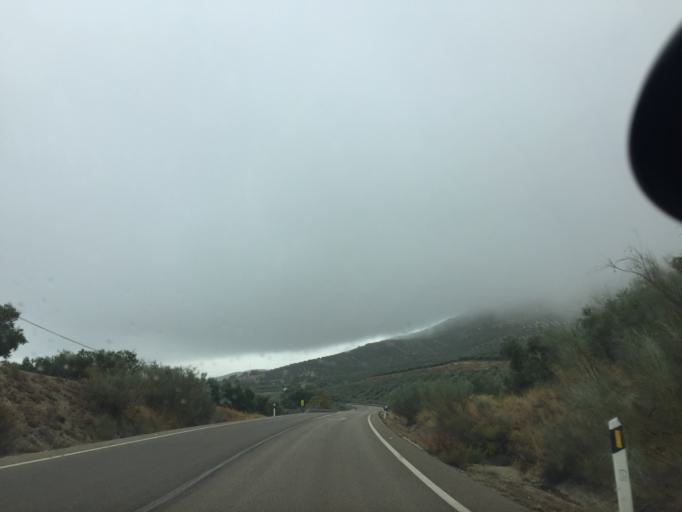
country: ES
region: Andalusia
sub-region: Provincia de Jaen
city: Jimena
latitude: 37.8475
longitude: -3.5016
